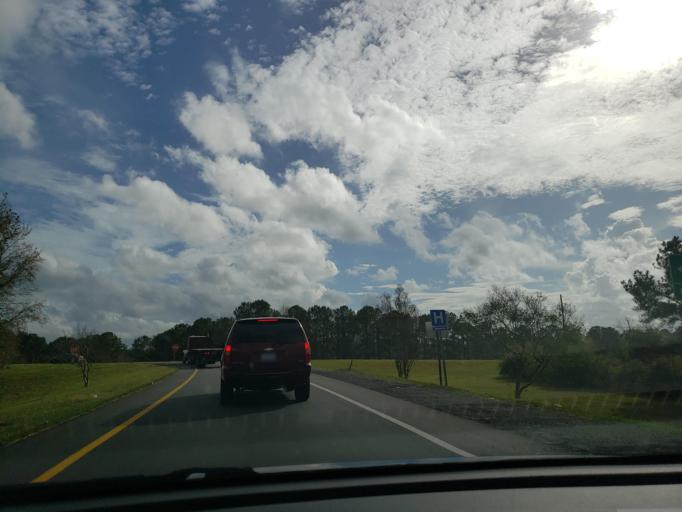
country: US
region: North Carolina
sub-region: Duplin County
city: Kenansville
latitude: 34.9179
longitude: -78.0260
